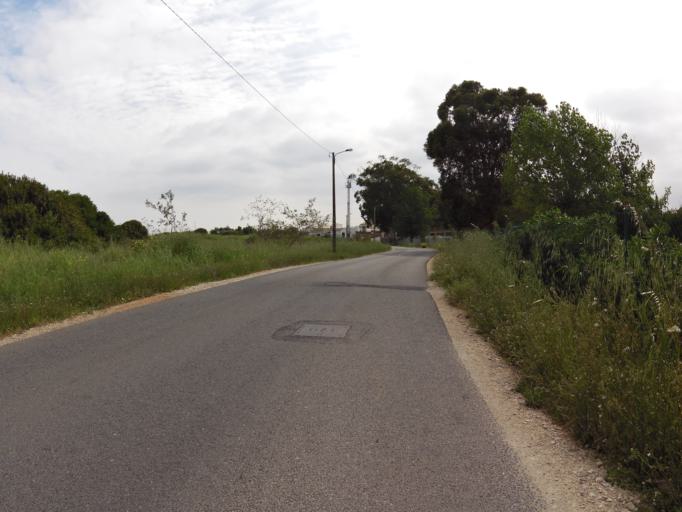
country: PT
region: Faro
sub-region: Silves
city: Armacao de Pera
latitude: 37.1085
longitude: -8.3500
